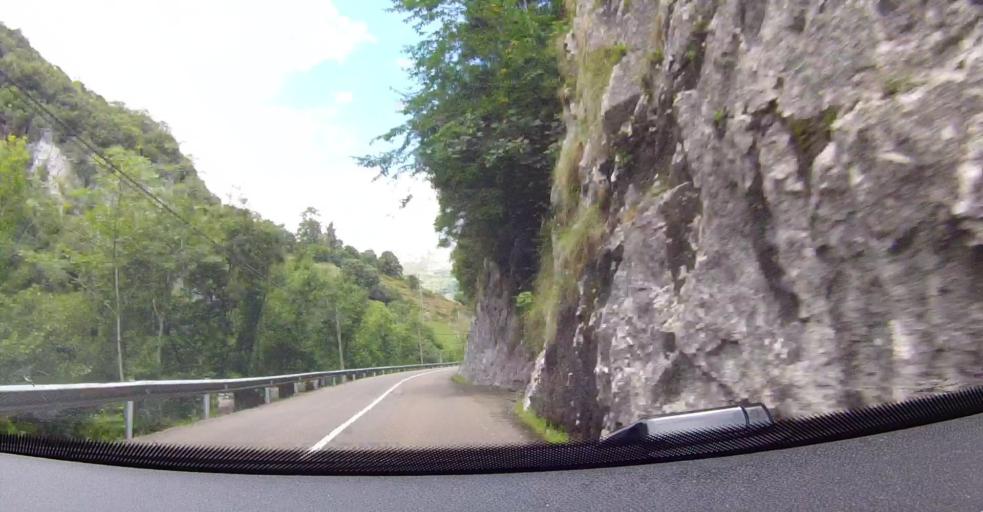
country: ES
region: Cantabria
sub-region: Provincia de Cantabria
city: Tresviso
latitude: 43.3132
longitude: -4.6090
